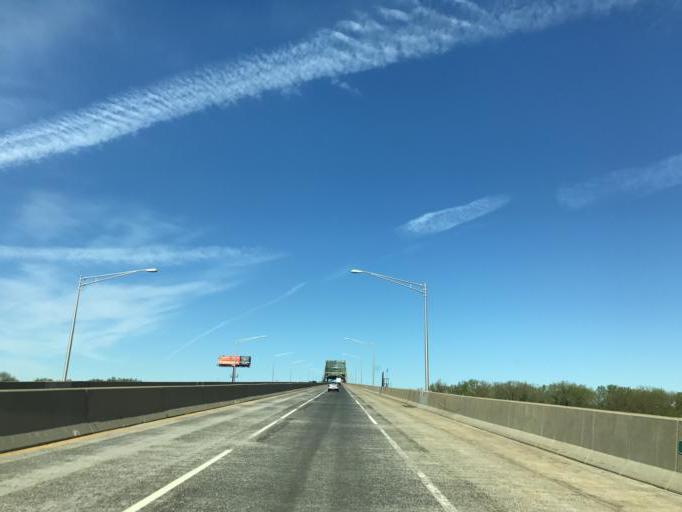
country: US
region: Pennsylvania
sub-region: Bucks County
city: Tullytown
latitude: 40.1146
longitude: -74.8217
